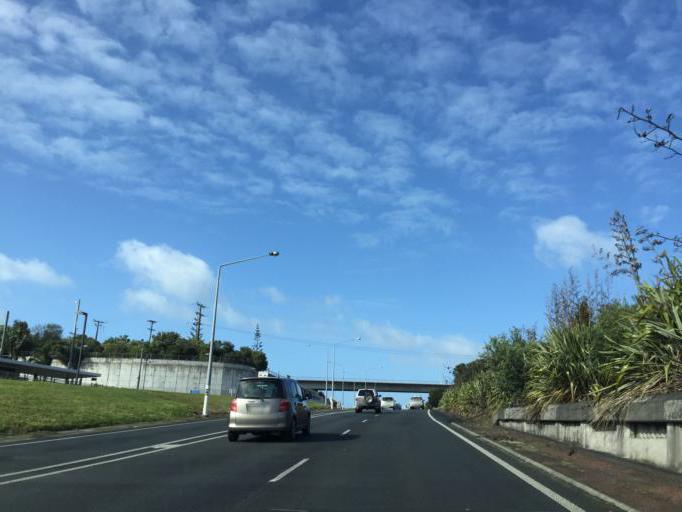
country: NZ
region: Auckland
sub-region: Auckland
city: Rothesay Bay
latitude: -36.7517
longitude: 174.7273
